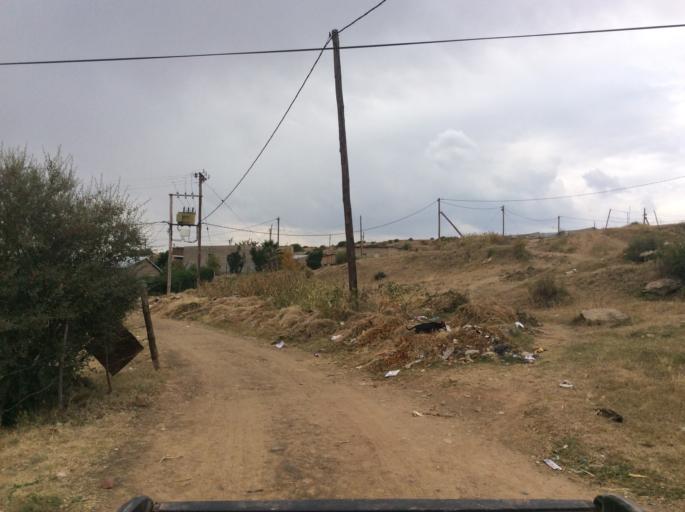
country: ZA
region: Orange Free State
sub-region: Xhariep District Municipality
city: Dewetsdorp
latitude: -29.5880
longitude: 26.6803
